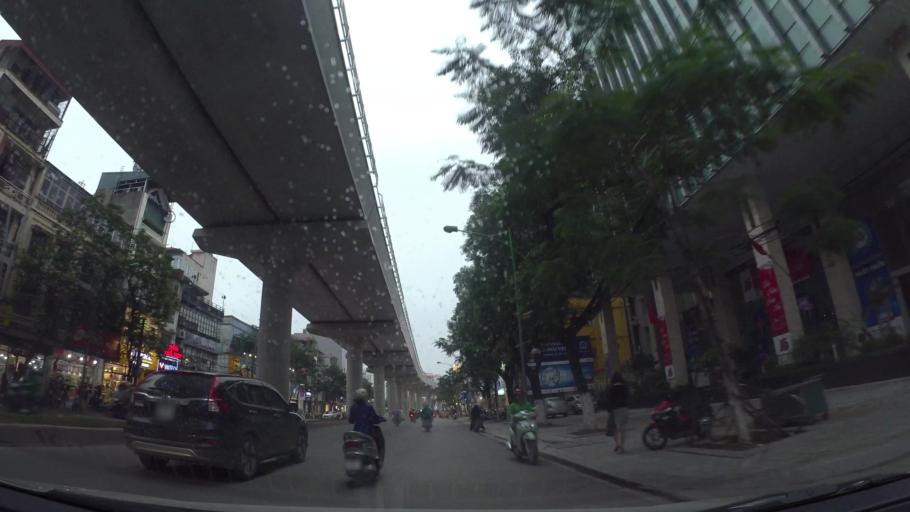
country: VN
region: Ha Noi
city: Cau Giay
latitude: 21.0347
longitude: 105.7952
